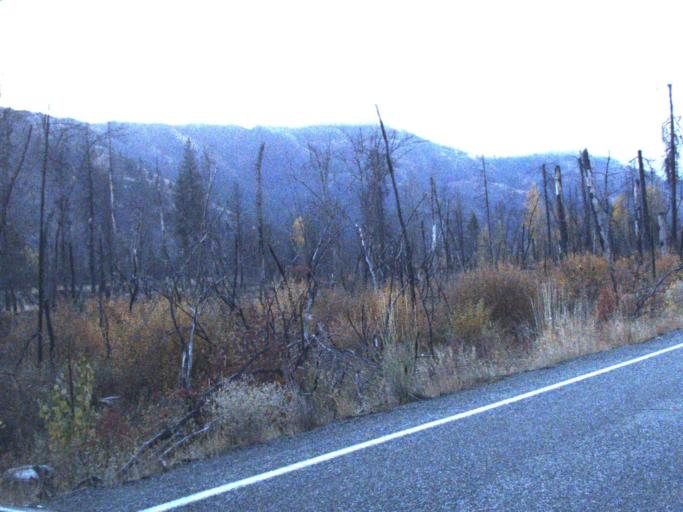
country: US
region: Washington
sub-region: Ferry County
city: Republic
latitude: 48.2624
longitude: -118.6923
